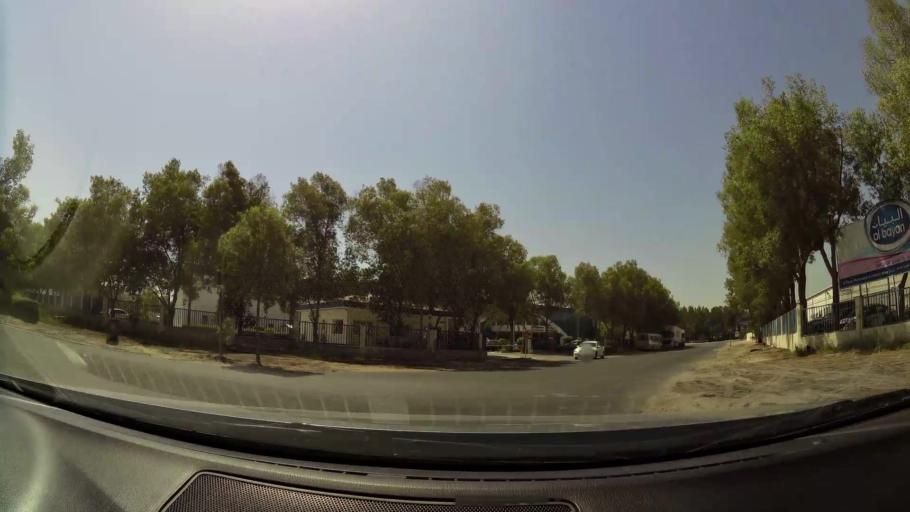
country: AE
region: Dubai
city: Dubai
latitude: 24.9772
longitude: 55.1509
